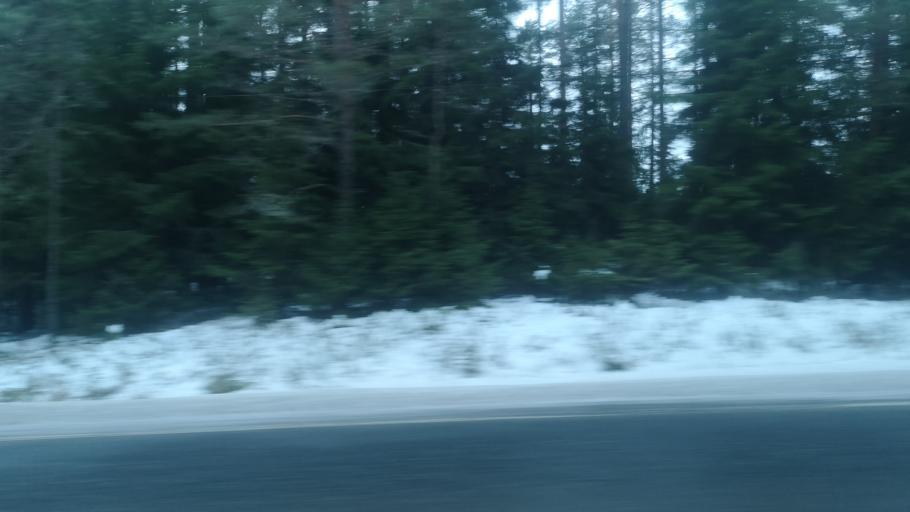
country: FI
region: Varsinais-Suomi
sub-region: Salo
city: Kisko
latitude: 60.2703
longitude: 23.4031
